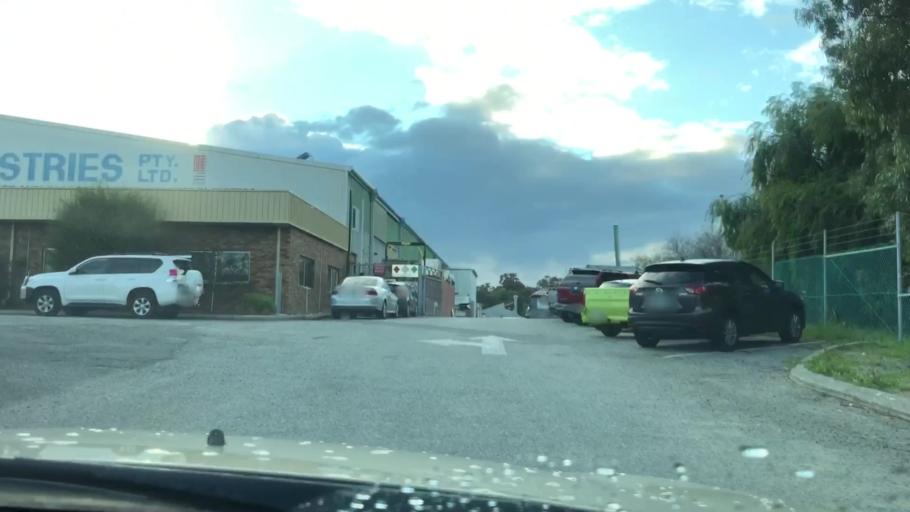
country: AU
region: Western Australia
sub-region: Melville
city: Myaree
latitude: -32.0419
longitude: 115.8225
